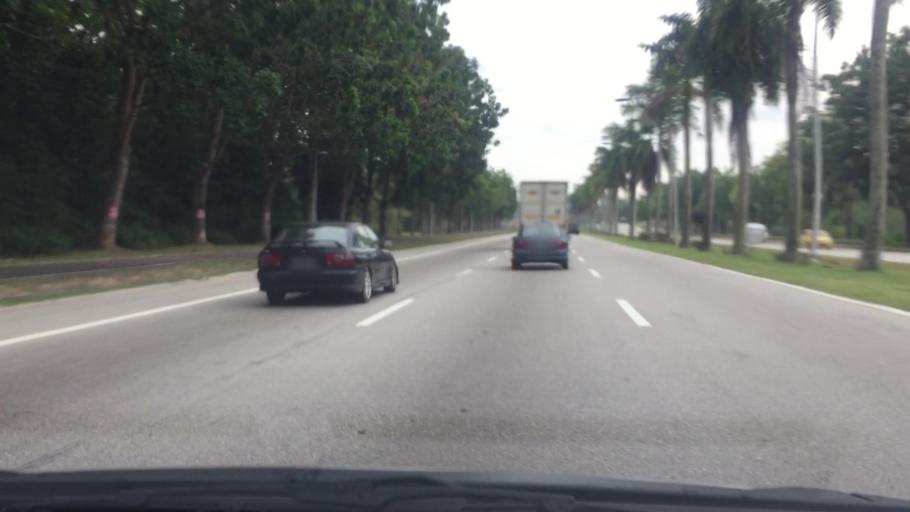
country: MY
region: Putrajaya
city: Putrajaya
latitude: 2.9026
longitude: 101.6582
